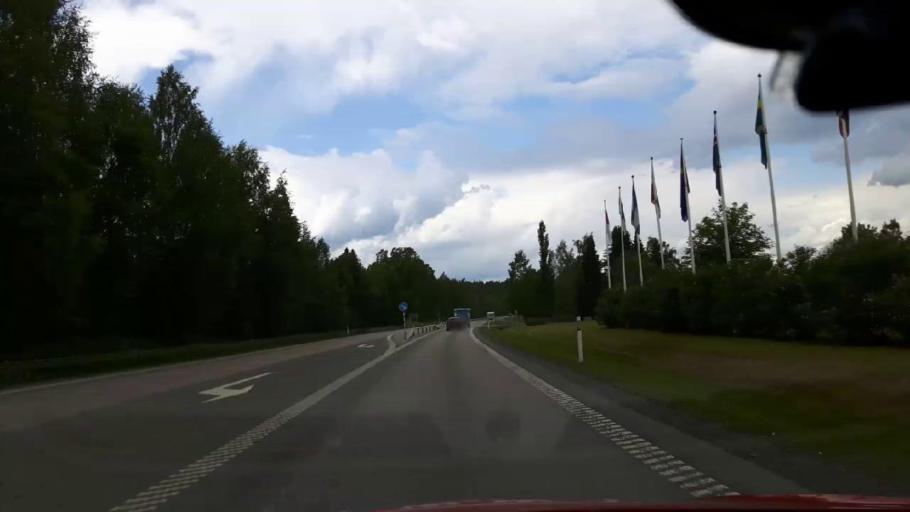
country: SE
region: Jaemtland
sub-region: Krokoms Kommun
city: Krokom
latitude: 63.3194
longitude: 14.4437
